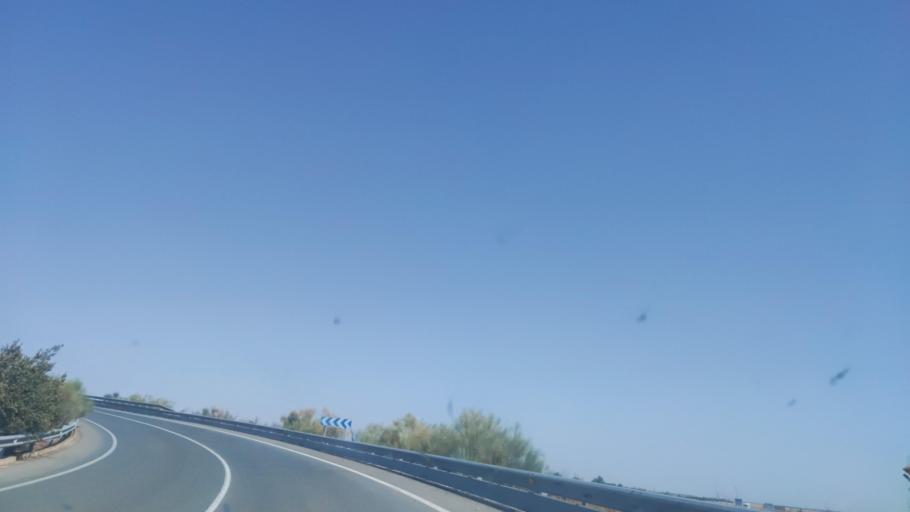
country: ES
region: Castille-La Mancha
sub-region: Provincia de Albacete
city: La Gineta
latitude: 39.1071
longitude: -1.9832
